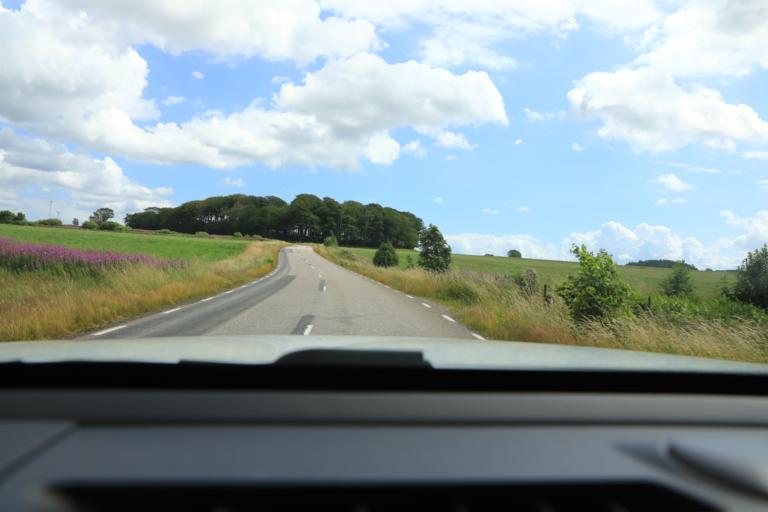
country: SE
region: Halland
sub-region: Varbergs Kommun
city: Tvaaker
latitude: 57.0332
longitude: 12.4574
